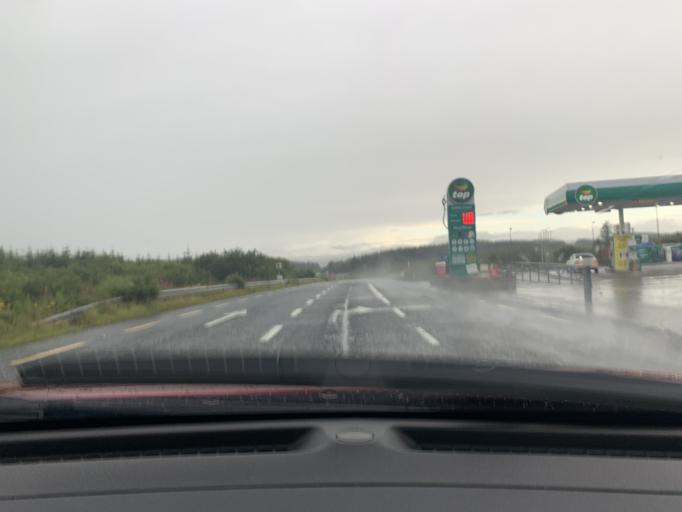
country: IE
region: Ulster
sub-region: County Donegal
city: Letterkenny
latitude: 54.8901
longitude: -7.7334
